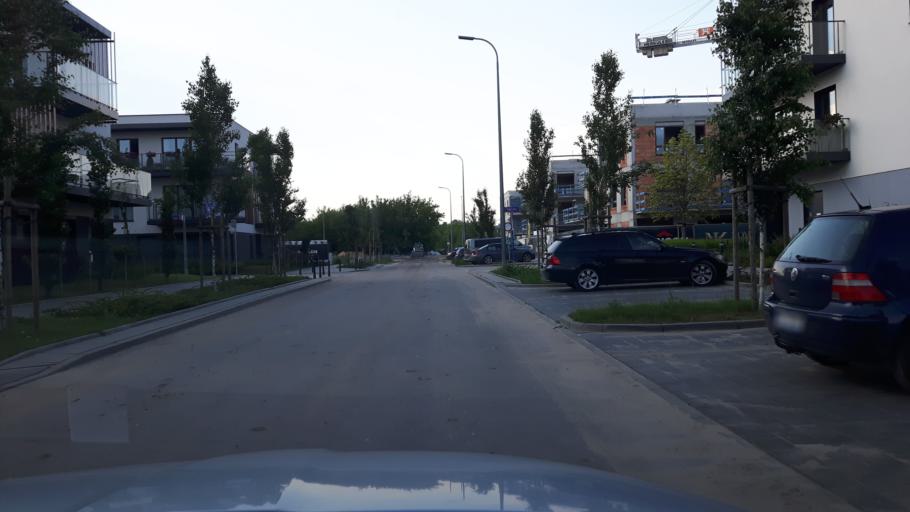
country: PL
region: Masovian Voivodeship
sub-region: Warszawa
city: Mokotow
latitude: 52.1834
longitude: 21.0391
